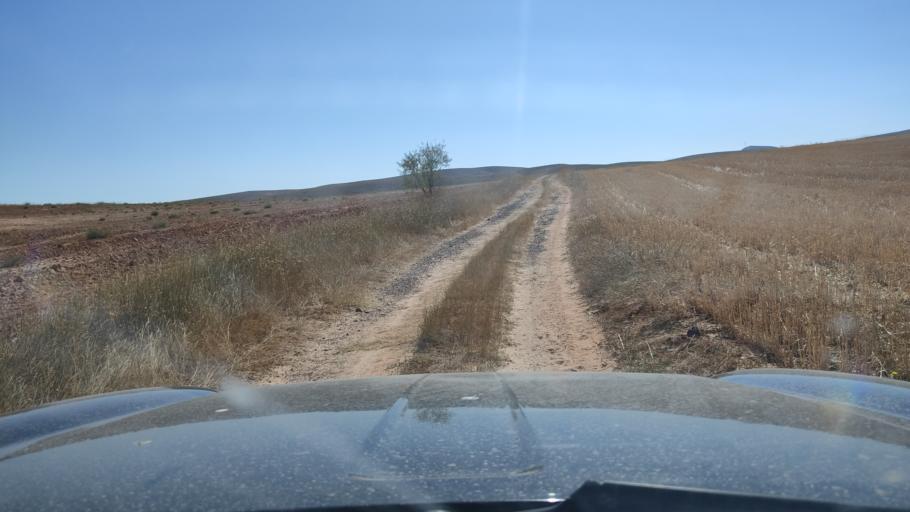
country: ES
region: Aragon
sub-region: Provincia de Teruel
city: Monforte de Moyuela
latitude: 41.0383
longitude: -0.9790
